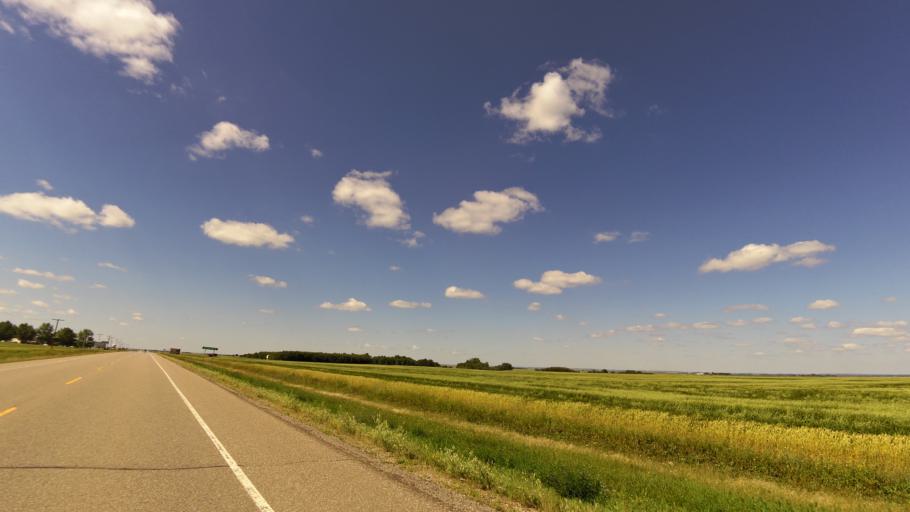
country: CA
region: Saskatchewan
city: Unity
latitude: 52.7549
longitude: -109.0133
